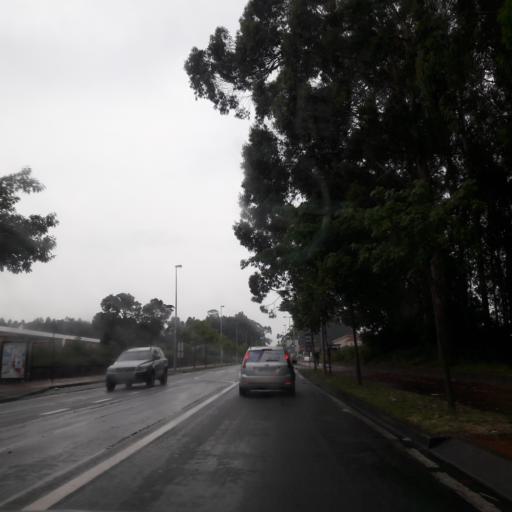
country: PT
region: Porto
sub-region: Vila do Conde
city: Arvore
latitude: 41.3227
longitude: -8.7142
